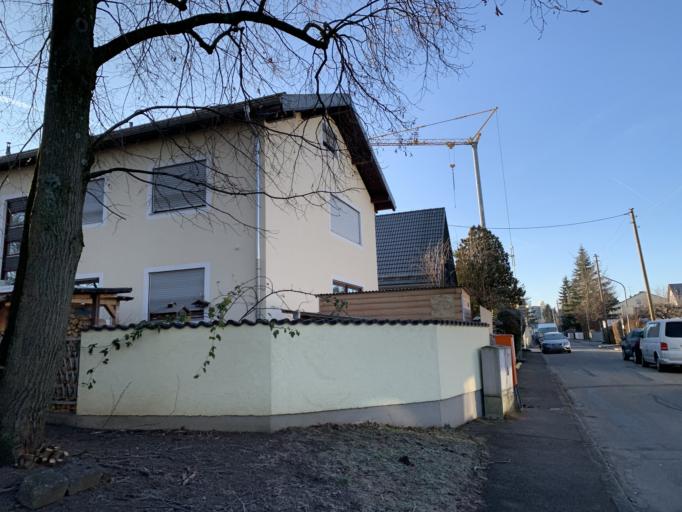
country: DE
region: Bavaria
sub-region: Upper Bavaria
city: Neubiberg
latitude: 48.1139
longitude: 11.6607
